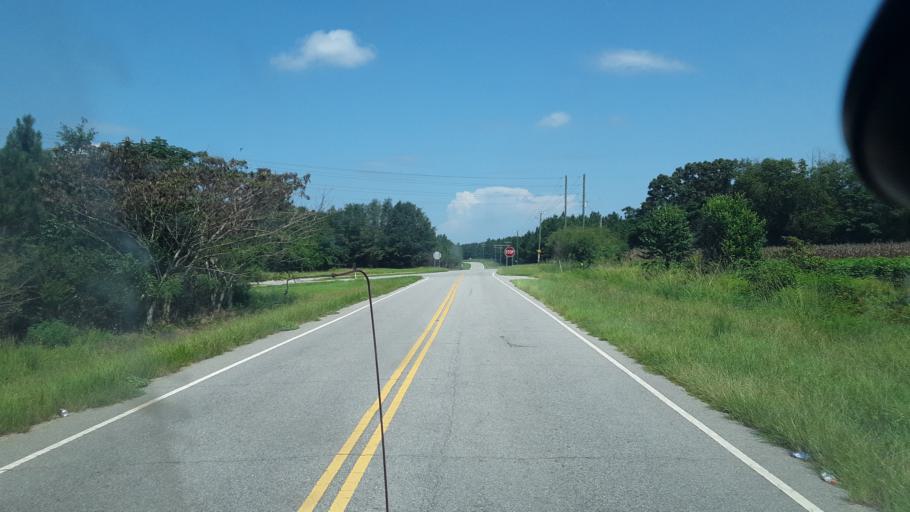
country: US
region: South Carolina
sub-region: Bamberg County
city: Bamberg
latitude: 33.4071
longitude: -81.0163
